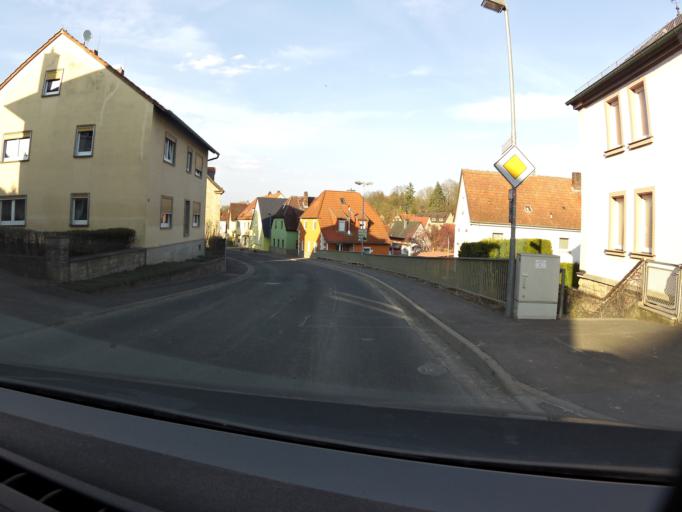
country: DE
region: Bavaria
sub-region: Regierungsbezirk Unterfranken
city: Kirchheim
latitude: 49.6569
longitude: 9.8597
